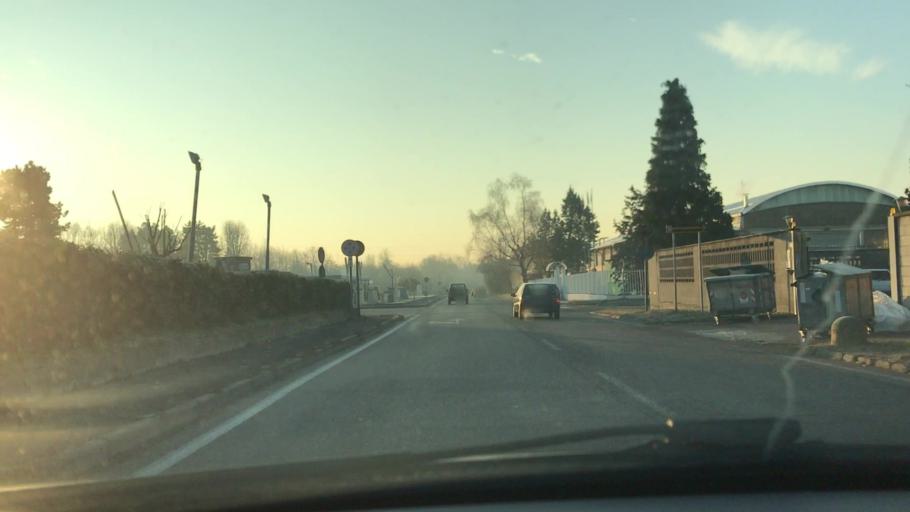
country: IT
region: Lombardy
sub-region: Citta metropolitana di Milano
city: Solaro
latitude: 45.6086
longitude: 9.0932
